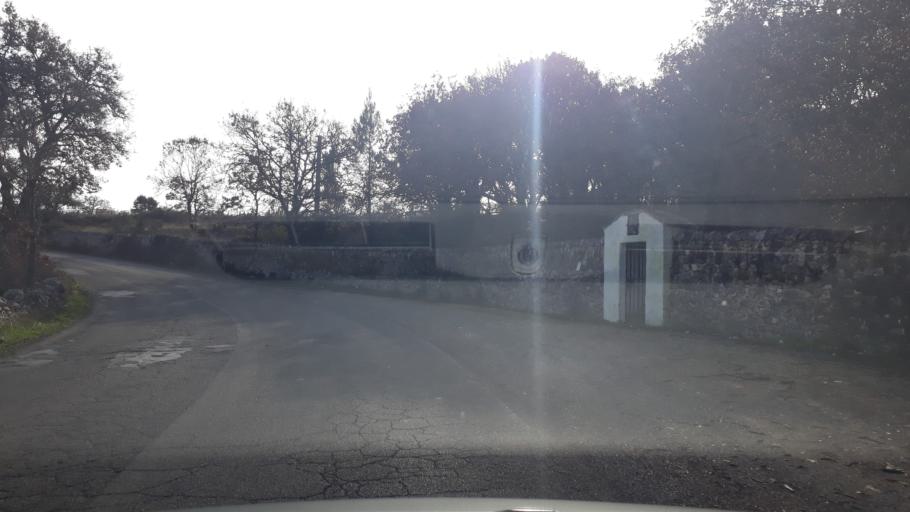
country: IT
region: Apulia
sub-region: Provincia di Taranto
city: Martina Franca
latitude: 40.6770
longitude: 17.3589
